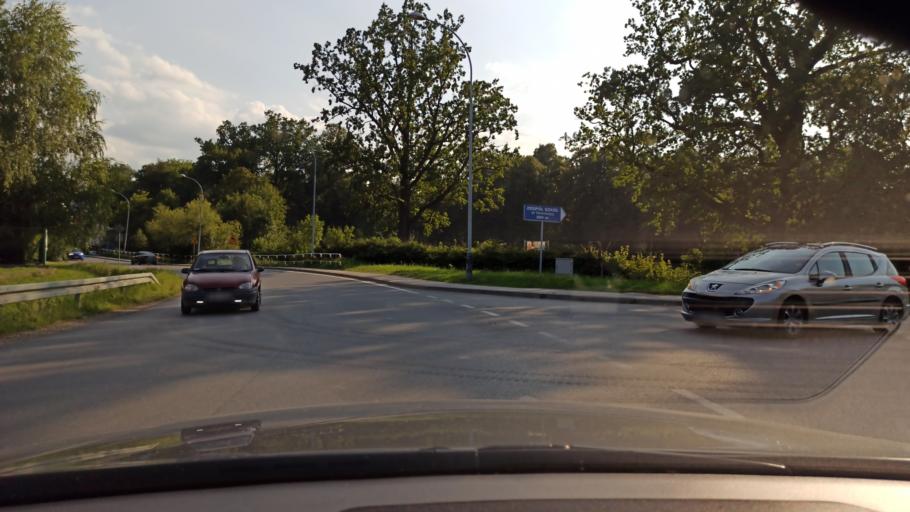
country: PL
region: Subcarpathian Voivodeship
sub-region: Powiat krosnienski
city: Miejsce Piastowe
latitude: 49.6035
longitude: 21.8015
